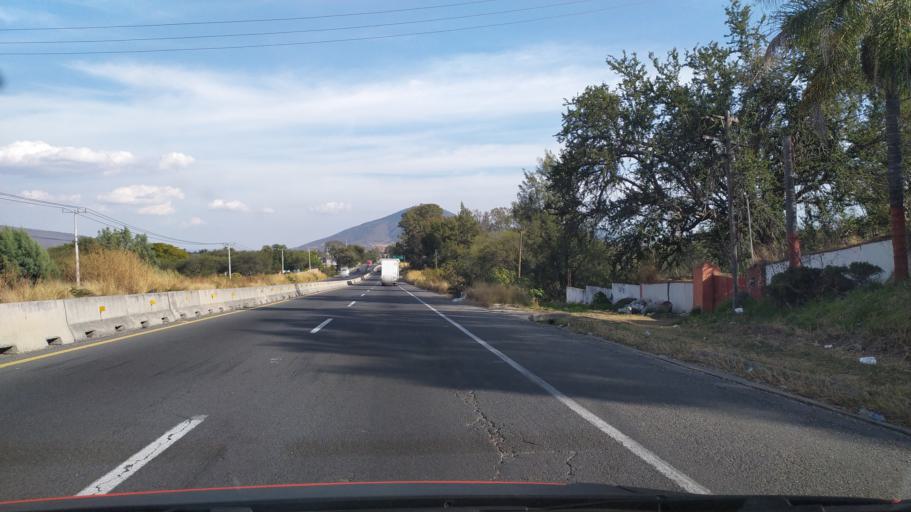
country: MX
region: Jalisco
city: Atequiza
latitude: 20.3994
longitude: -103.1547
